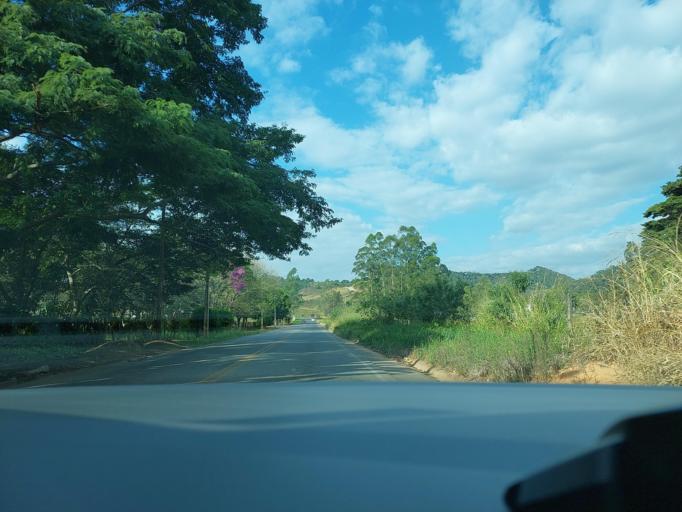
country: BR
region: Minas Gerais
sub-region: Vicosa
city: Vicosa
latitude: -20.8323
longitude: -42.7911
